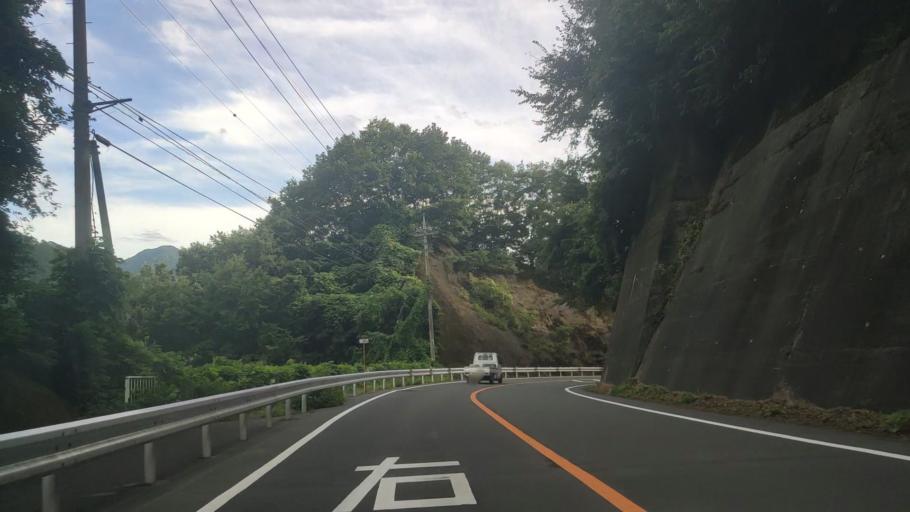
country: JP
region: Gunma
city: Omamacho-omama
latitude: 36.5476
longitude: 139.3720
